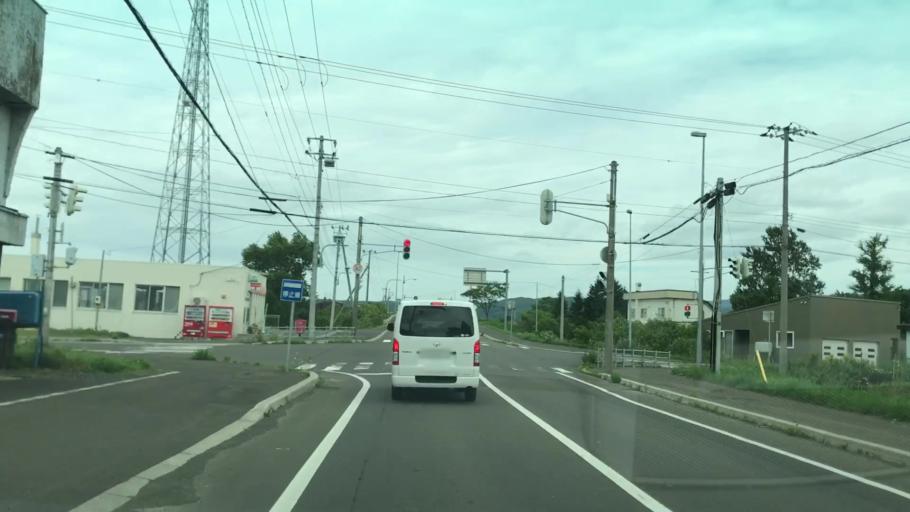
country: JP
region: Hokkaido
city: Iwanai
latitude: 43.0161
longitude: 140.5682
